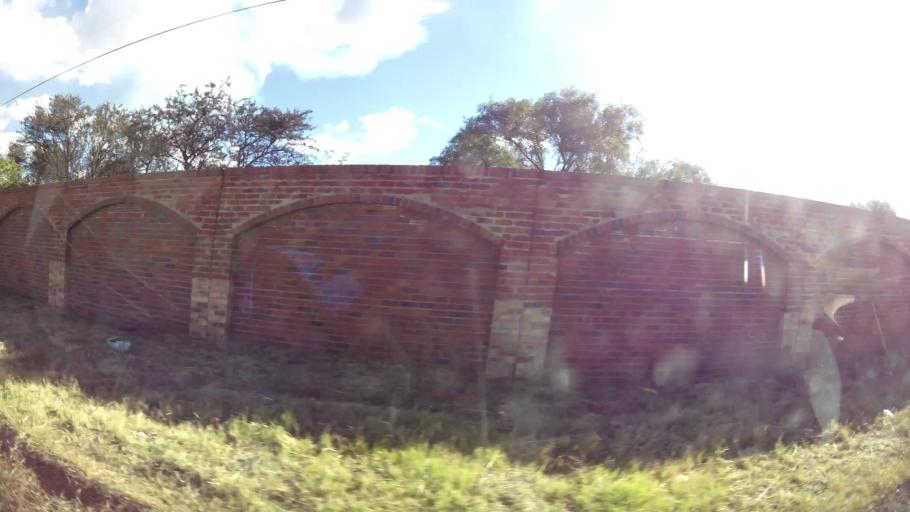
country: ZA
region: North-West
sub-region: Dr Kenneth Kaunda District Municipality
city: Klerksdorp
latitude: -26.8182
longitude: 26.6794
